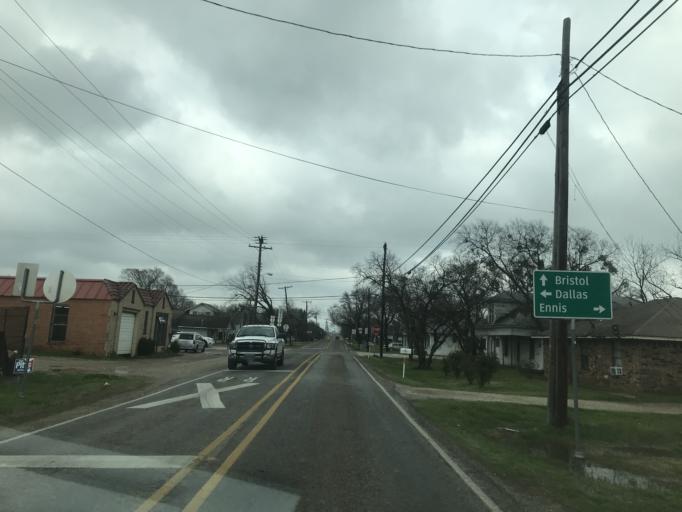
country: US
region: Texas
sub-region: Ellis County
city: Palmer
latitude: 32.4315
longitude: -96.6671
